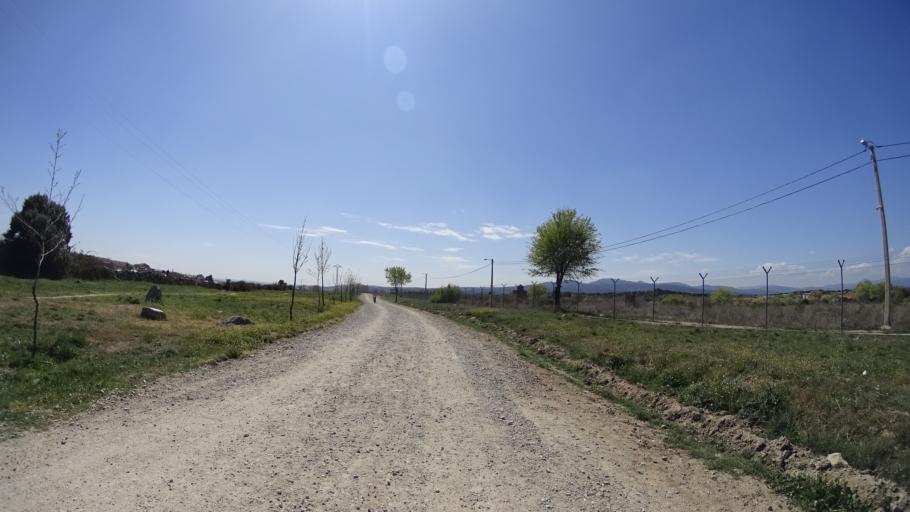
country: ES
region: Madrid
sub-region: Provincia de Madrid
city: Colmenar Viejo
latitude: 40.6769
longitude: -3.7833
